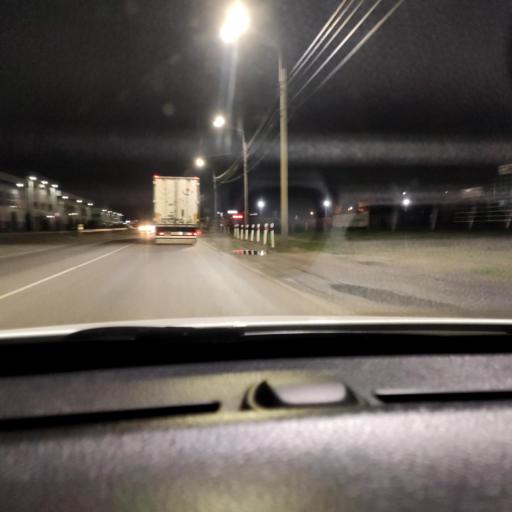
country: RU
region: Voronezj
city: Maslovka
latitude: 51.6375
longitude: 39.2920
